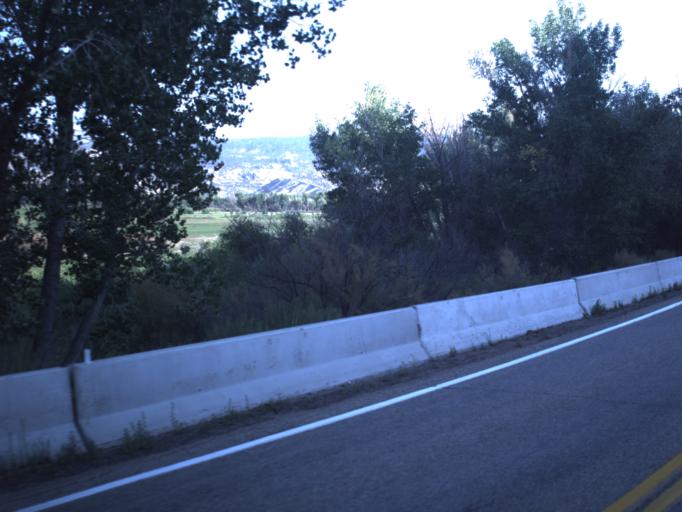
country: US
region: Utah
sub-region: Uintah County
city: Vernal
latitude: 40.5235
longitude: -109.5216
